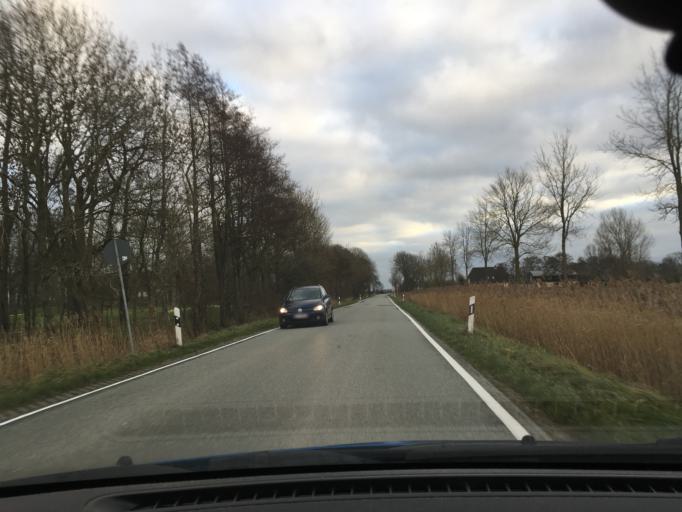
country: DE
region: Schleswig-Holstein
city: Norderwohrden
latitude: 54.1968
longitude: 9.0331
